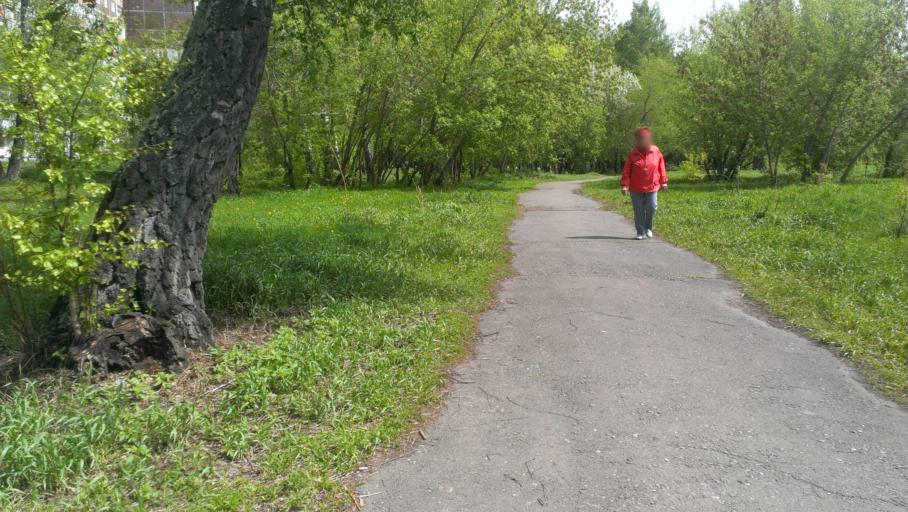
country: RU
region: Altai Krai
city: Novosilikatnyy
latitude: 53.3611
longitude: 83.6676
